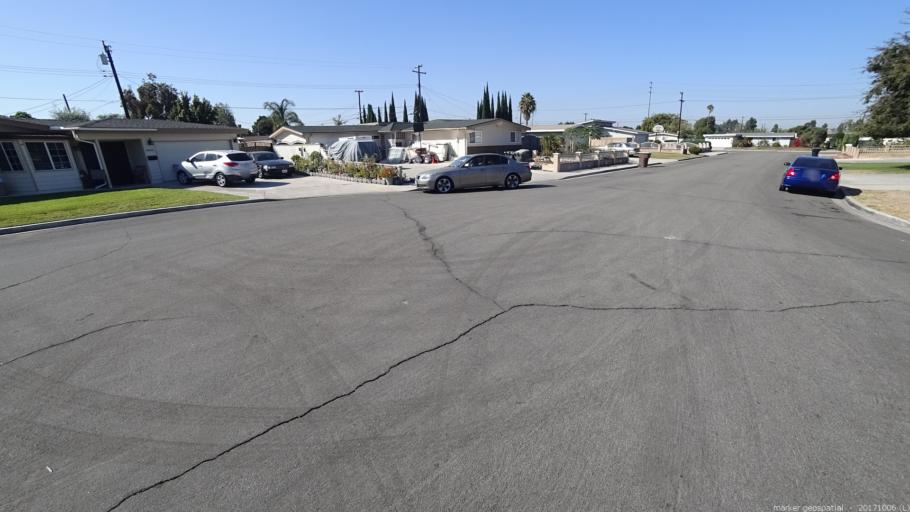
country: US
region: California
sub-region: Orange County
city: Stanton
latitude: 33.7852
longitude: -117.9782
